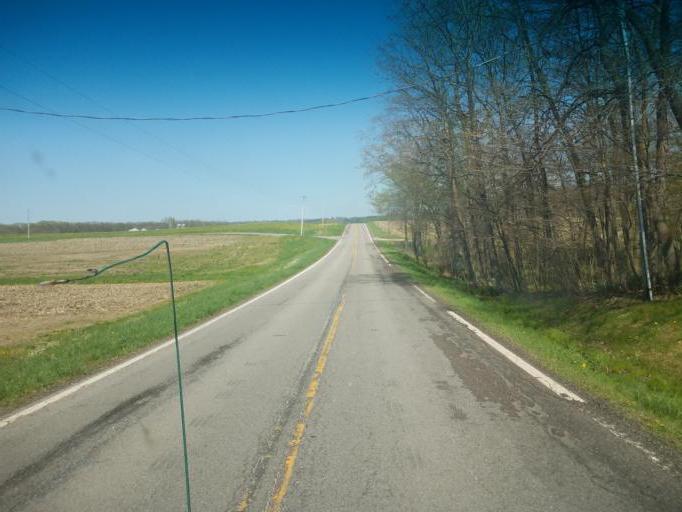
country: US
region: Ohio
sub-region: Wayne County
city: West Salem
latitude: 40.9305
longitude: -82.0348
